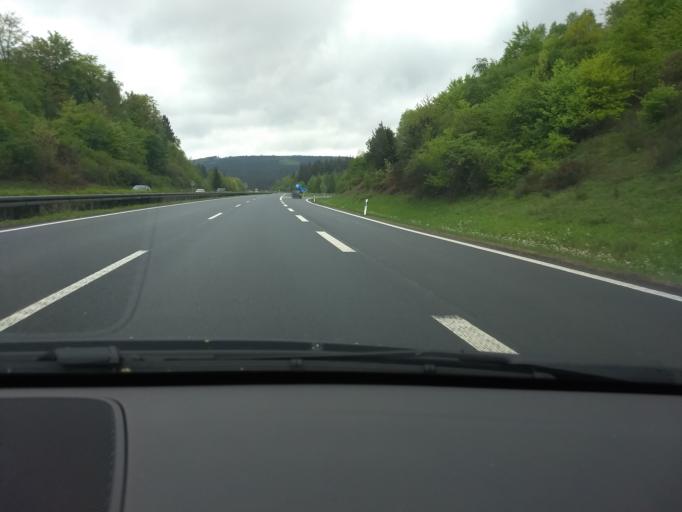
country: DE
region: North Rhine-Westphalia
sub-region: Regierungsbezirk Arnsberg
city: Arnsberg
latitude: 51.4197
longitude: 8.0617
